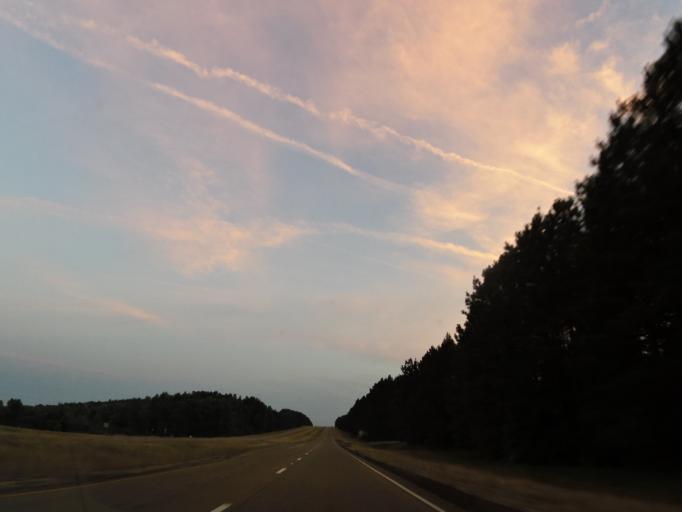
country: US
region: Mississippi
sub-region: Lauderdale County
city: Meridian Station
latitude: 32.5878
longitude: -88.5021
